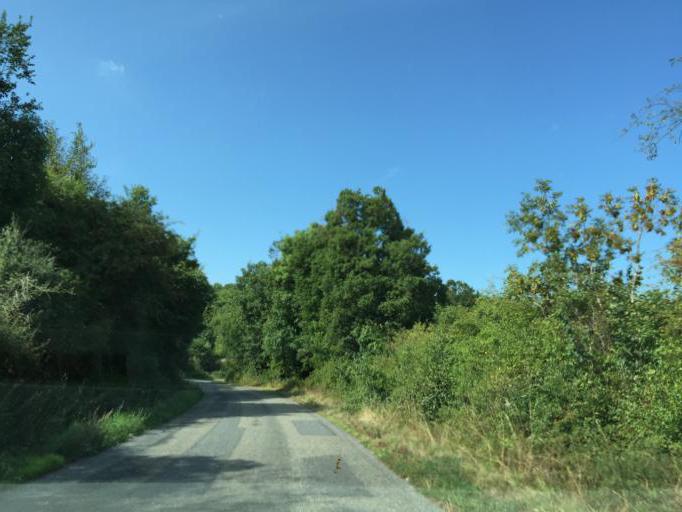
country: FR
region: Midi-Pyrenees
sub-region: Departement de l'Aveyron
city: Sainte-Radegonde
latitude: 44.3309
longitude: 2.6201
